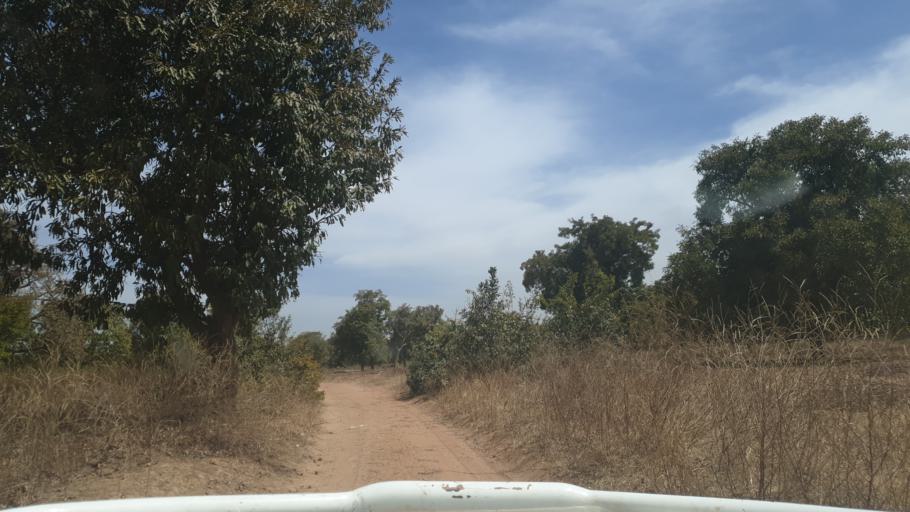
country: ML
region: Sikasso
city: Yorosso
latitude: 12.2886
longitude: -4.6713
